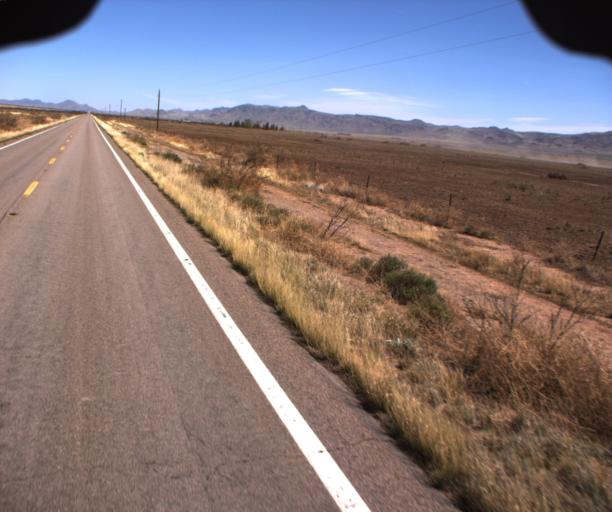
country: US
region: Arizona
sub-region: Cochise County
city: Douglas
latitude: 31.7232
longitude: -109.1101
